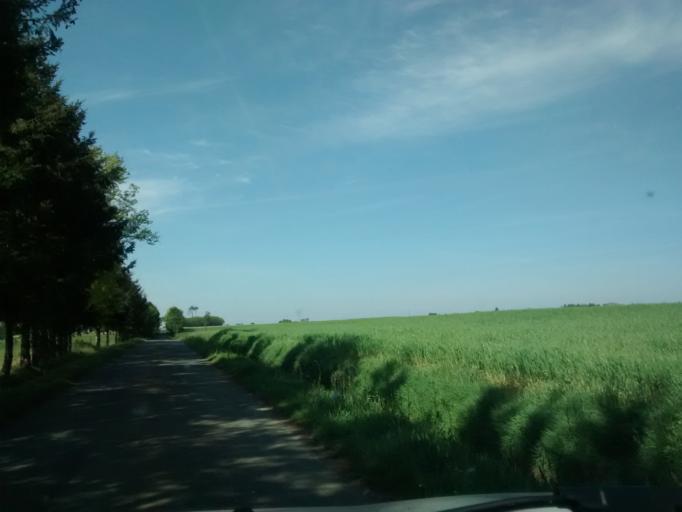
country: FR
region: Brittany
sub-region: Departement d'Ille-et-Vilaine
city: Grand-Fougeray
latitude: 47.7774
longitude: -1.7606
